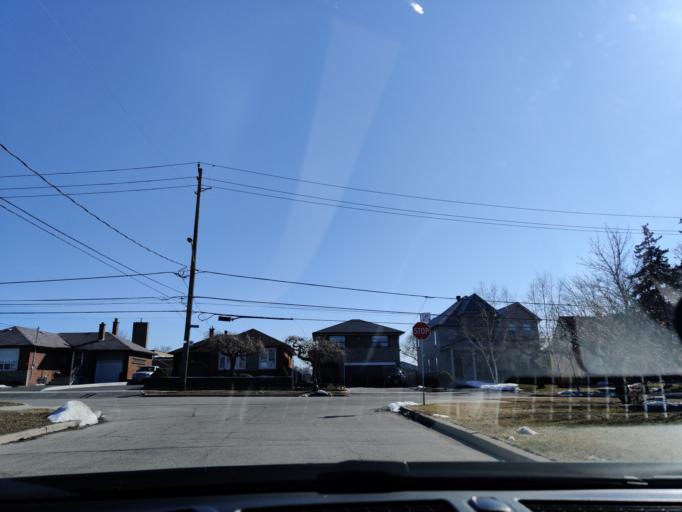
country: CA
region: Ontario
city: Toronto
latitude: 43.7192
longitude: -79.4764
